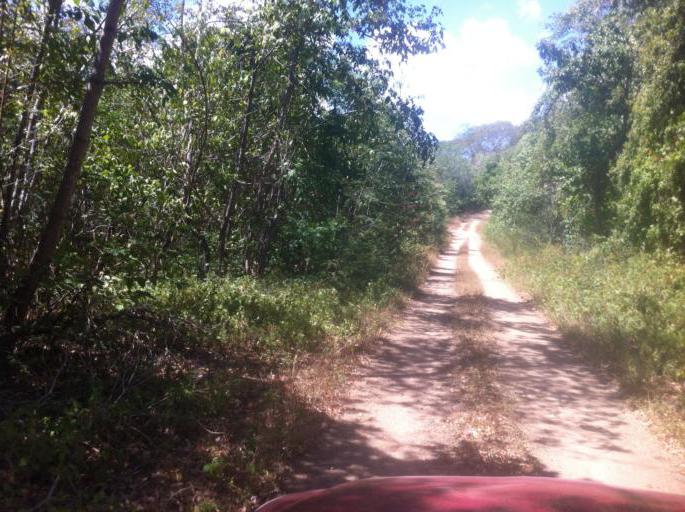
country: NI
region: Rivas
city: Tola
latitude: 11.3342
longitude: -85.9536
